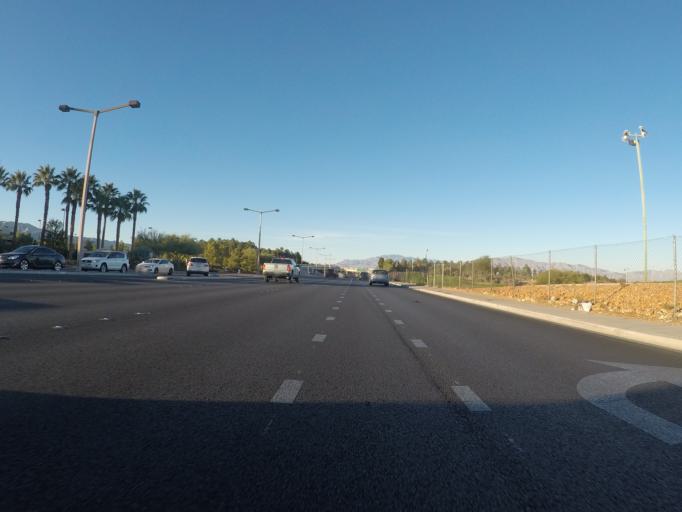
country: US
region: Nevada
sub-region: Clark County
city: Summerlin South
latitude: 36.1748
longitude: -115.2870
